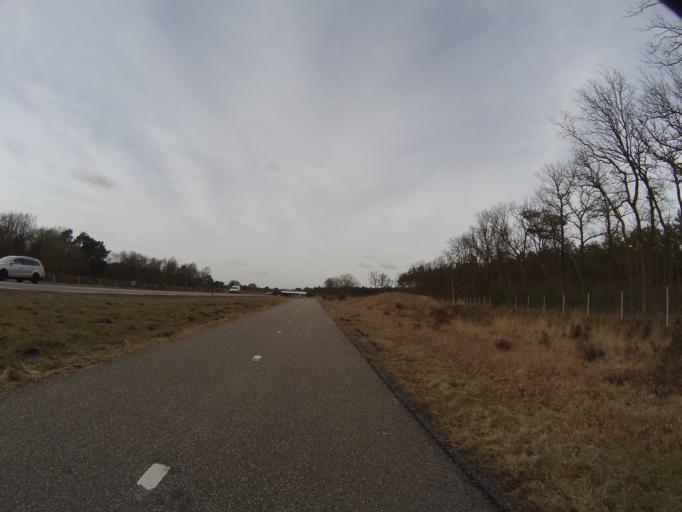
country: NL
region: Utrecht
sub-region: Gemeente Utrechtse Heuvelrug
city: Maarn
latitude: 52.1039
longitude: 5.3626
